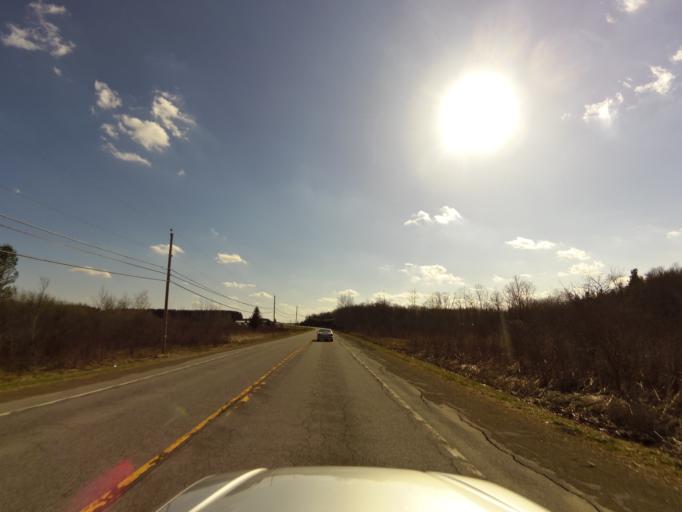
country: US
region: New York
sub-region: Wyoming County
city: Castile
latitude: 42.5700
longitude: -78.1358
